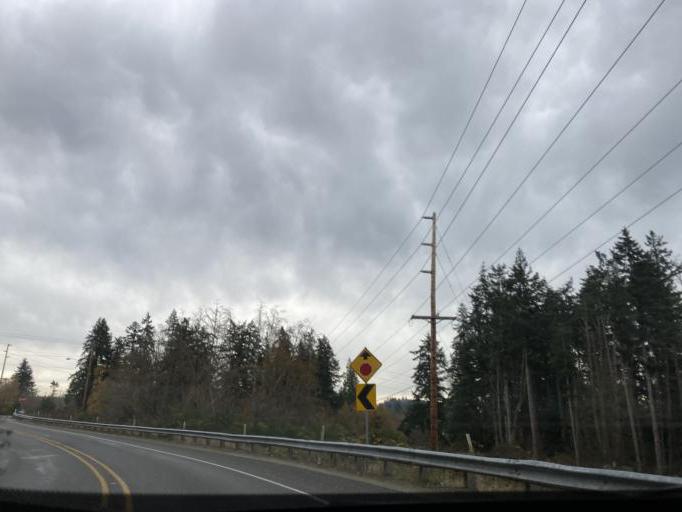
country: US
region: Washington
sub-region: Island County
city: Freeland
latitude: 48.0146
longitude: -122.5470
